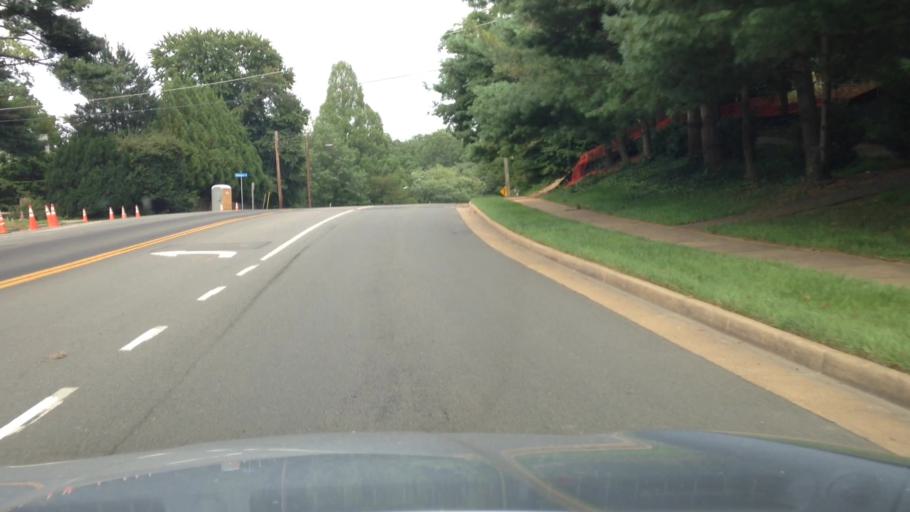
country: US
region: Virginia
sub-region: Fairfax County
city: Pimmit Hills
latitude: 38.9105
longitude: -77.1801
